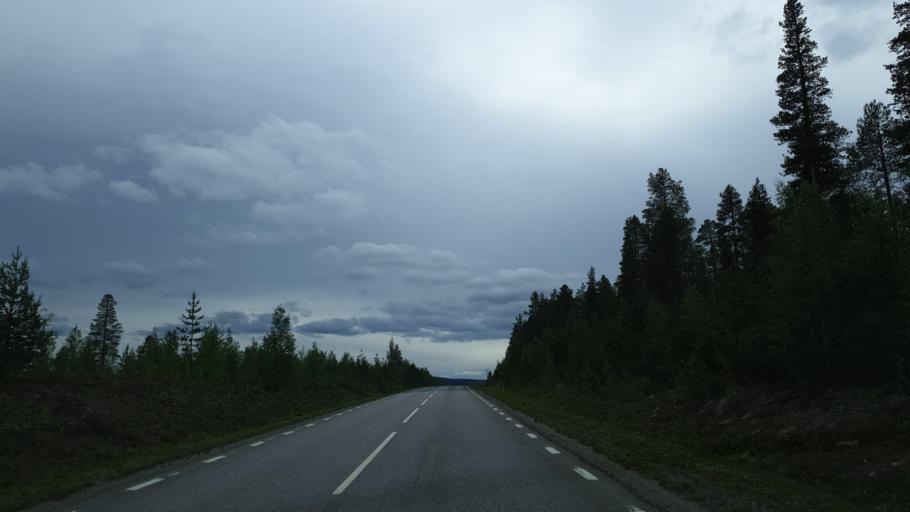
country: SE
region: Vaesterbotten
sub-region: Sorsele Kommun
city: Sorsele
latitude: 65.5359
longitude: 17.3961
